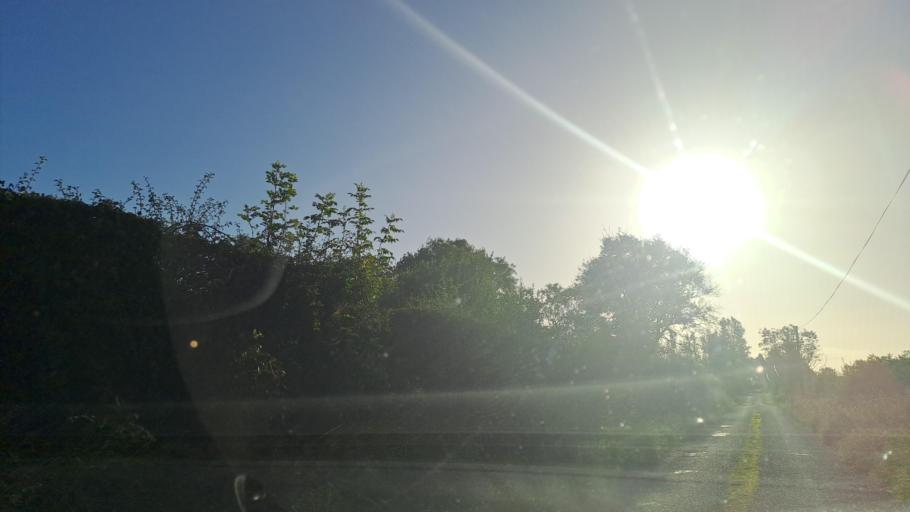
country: IE
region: Ulster
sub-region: An Cabhan
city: Kingscourt
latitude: 53.9820
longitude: -6.8560
